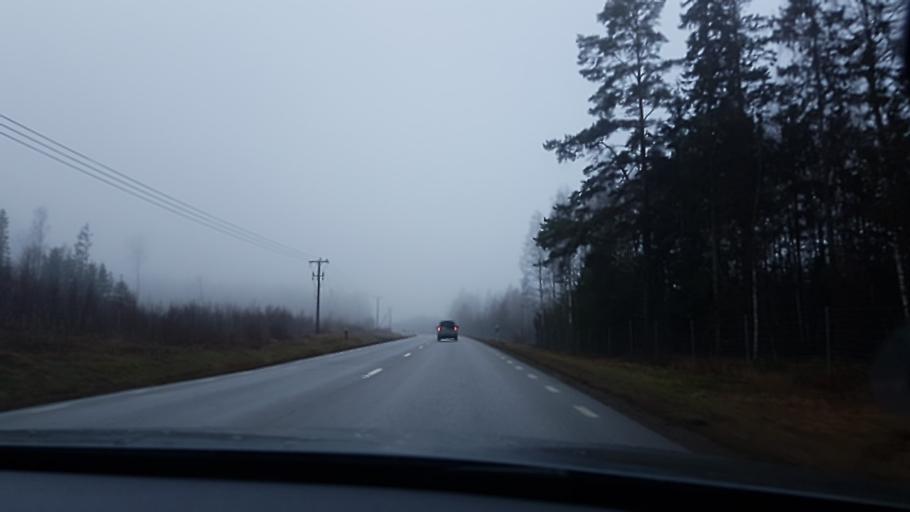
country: SE
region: Vaestra Goetaland
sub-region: Gullspangs Kommun
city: Gullspang
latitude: 58.9347
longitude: 14.0367
